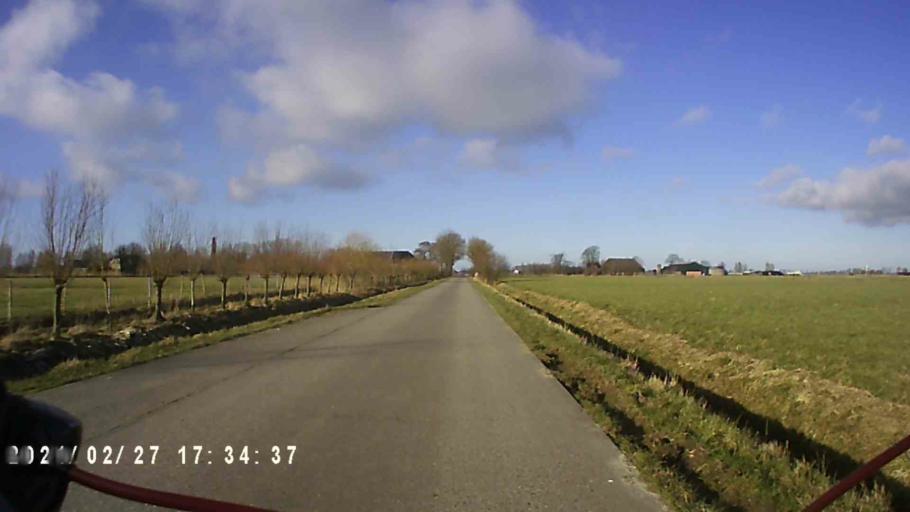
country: NL
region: Groningen
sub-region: Gemeente Bedum
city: Bedum
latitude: 53.3329
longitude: 6.5695
